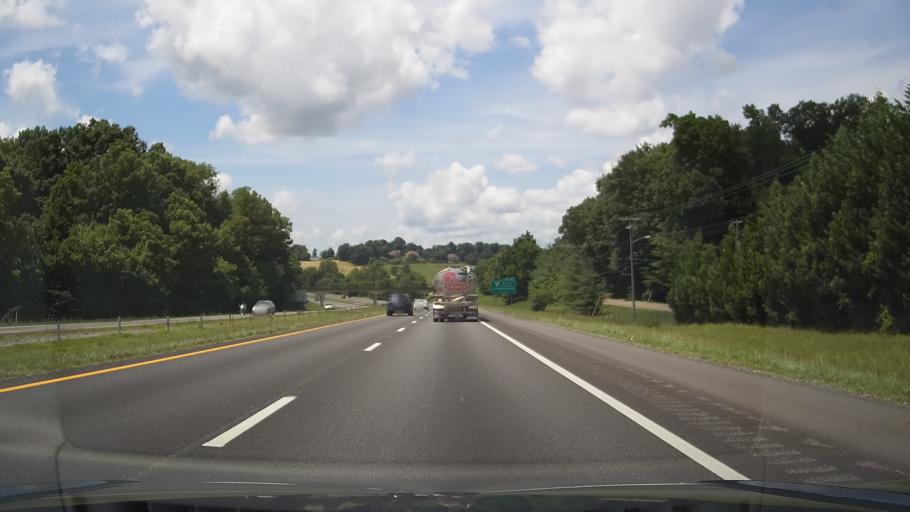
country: US
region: Tennessee
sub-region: Washington County
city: Oak Grove
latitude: 36.3653
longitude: -82.4115
